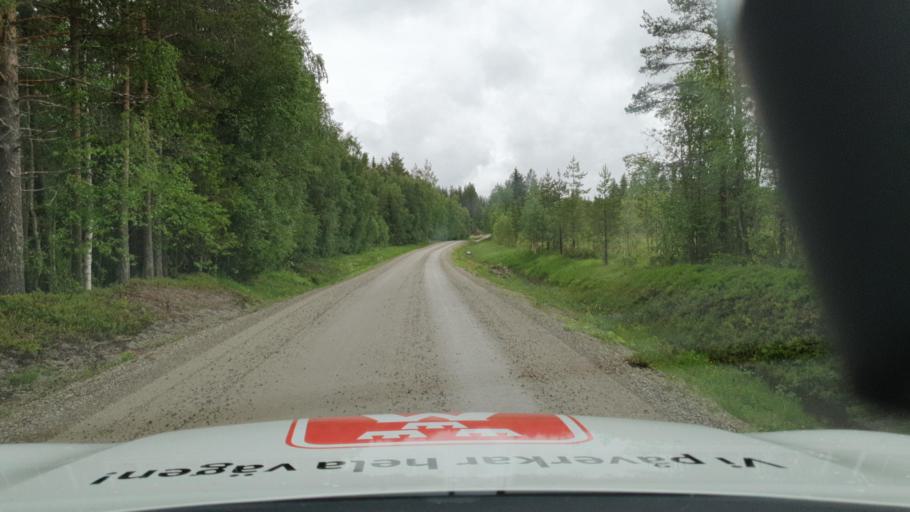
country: SE
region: Vaesterbotten
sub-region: Dorotea Kommun
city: Dorotea
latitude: 63.9987
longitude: 16.7995
